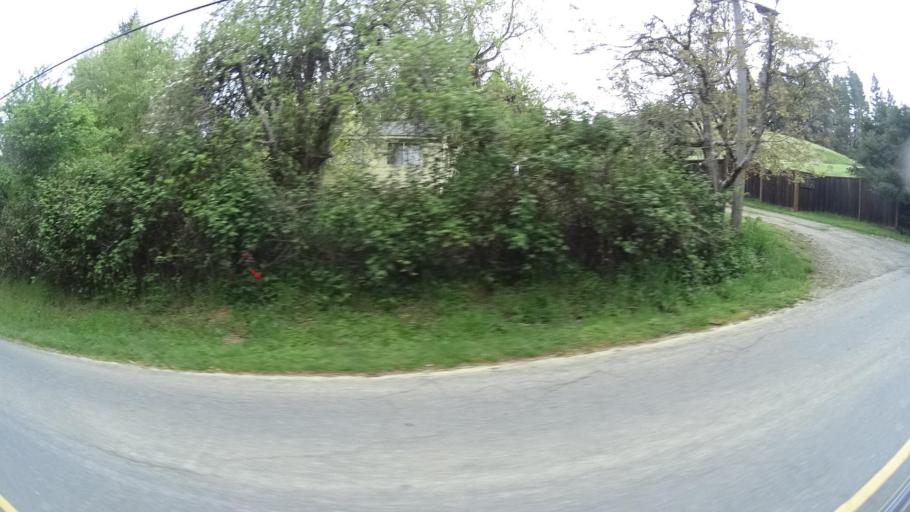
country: US
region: California
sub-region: Humboldt County
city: Redway
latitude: 40.2932
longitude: -123.8216
